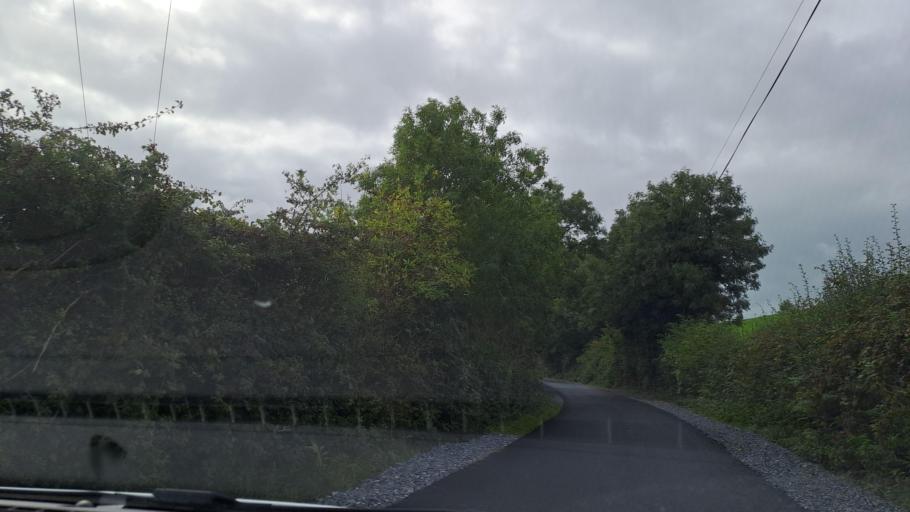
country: IE
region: Ulster
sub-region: County Monaghan
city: Carrickmacross
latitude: 53.9877
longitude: -6.7763
